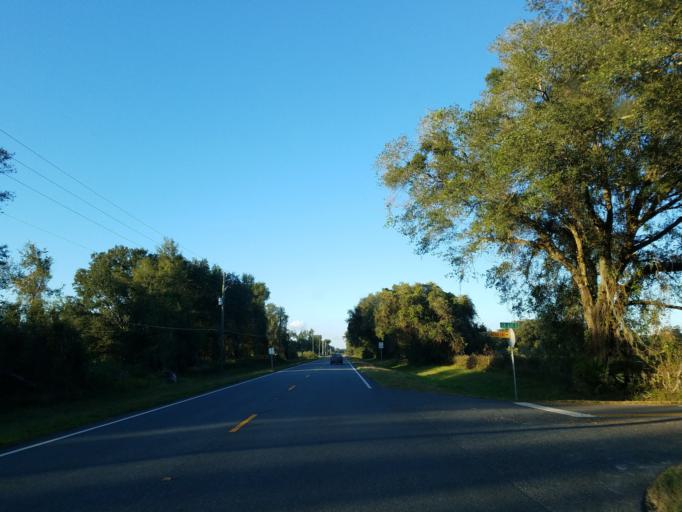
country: US
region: Florida
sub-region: Sumter County
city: Bushnell
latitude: 28.6251
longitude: -82.2037
